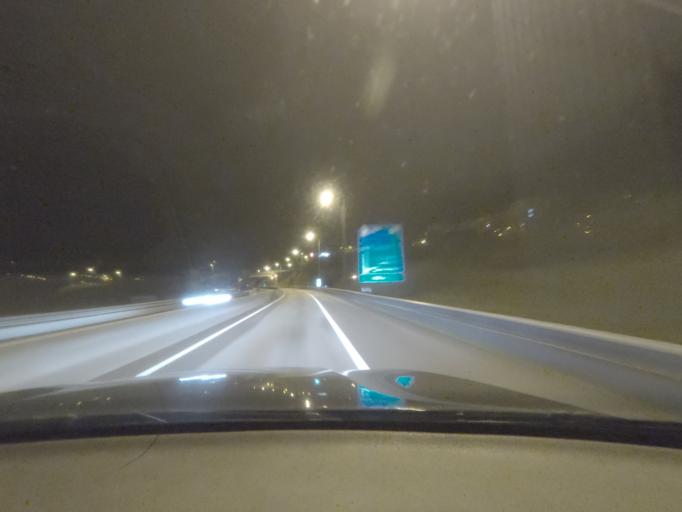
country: PT
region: Vila Real
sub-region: Vila Real
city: Vila Real
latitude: 41.2987
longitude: -7.7545
